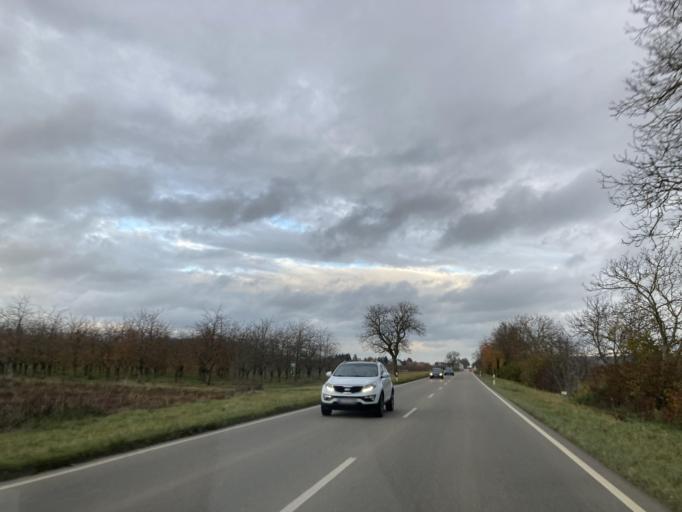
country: DE
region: Baden-Wuerttemberg
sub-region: Freiburg Region
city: Auggen
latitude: 47.7793
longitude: 7.5856
